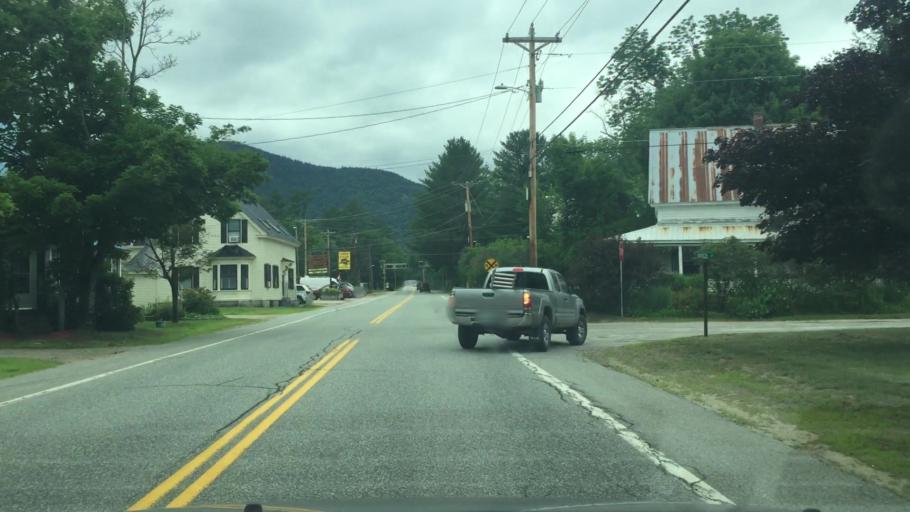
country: US
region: New Hampshire
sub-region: Carroll County
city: North Conway
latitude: 44.0775
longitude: -71.2859
